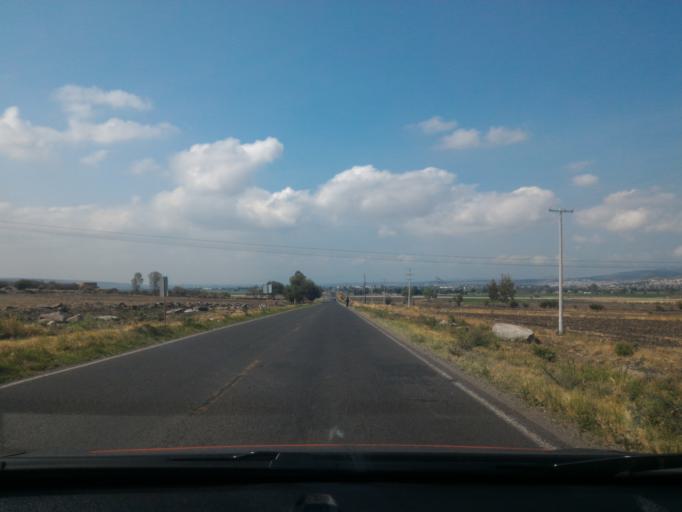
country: MX
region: Guanajuato
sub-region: Penjamo
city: Estacion la Piedad
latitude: 20.4061
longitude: -101.9984
